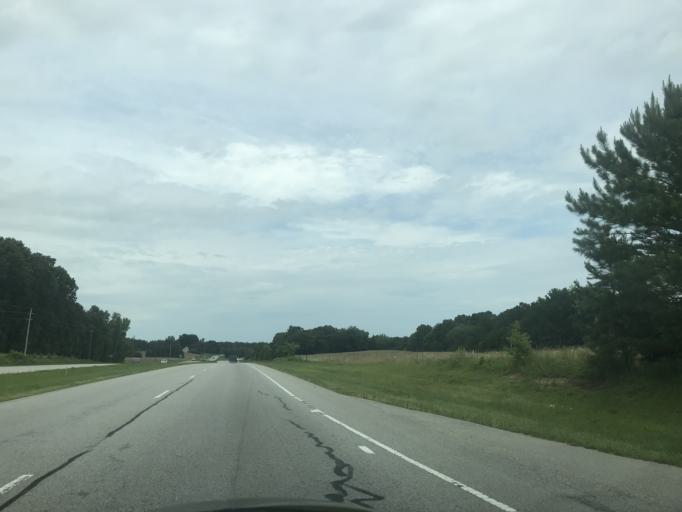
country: US
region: North Carolina
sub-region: Franklin County
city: Franklinton
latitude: 36.1509
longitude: -78.4522
